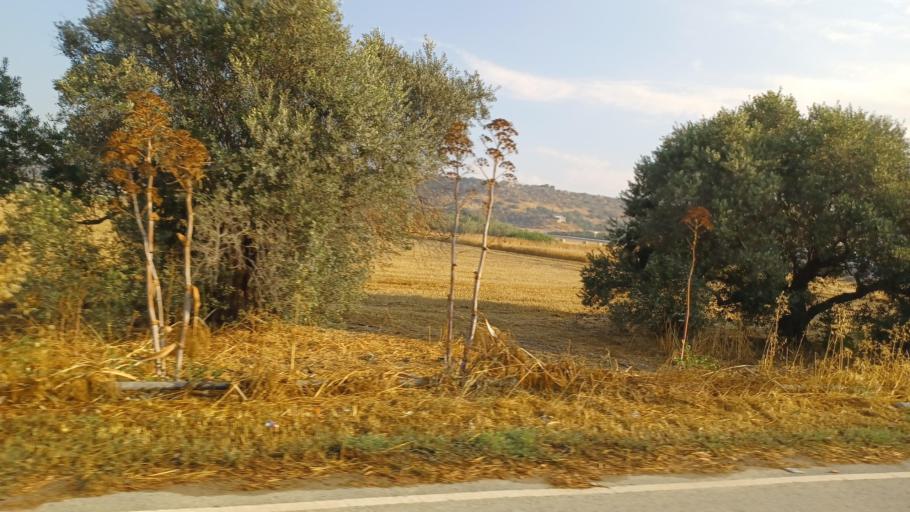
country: CY
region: Larnaka
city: Pyla
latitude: 35.0087
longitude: 33.7003
